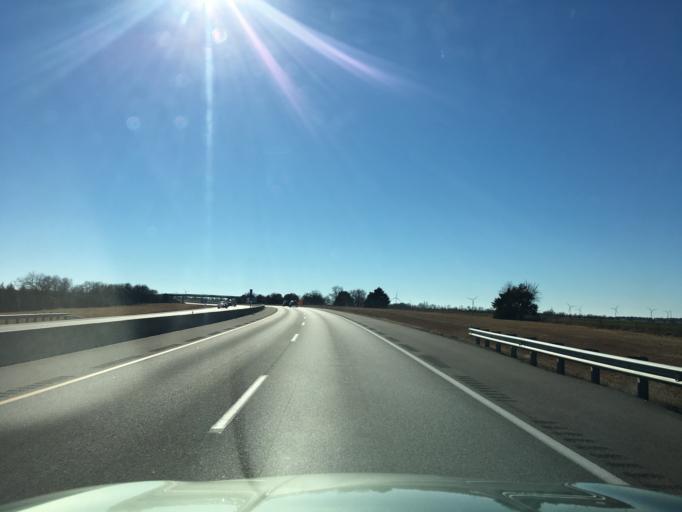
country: US
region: Kansas
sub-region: Sumner County
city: Wellington
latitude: 37.1934
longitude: -97.3417
